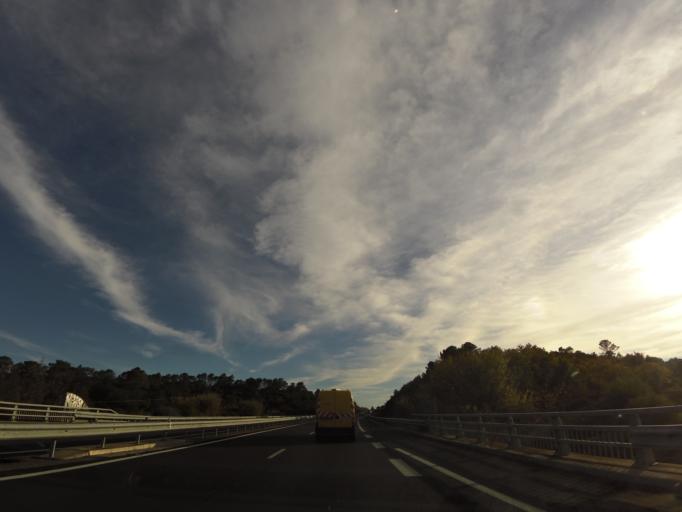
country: FR
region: Languedoc-Roussillon
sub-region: Departement du Gard
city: Vezenobres
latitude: 44.0593
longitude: 4.1229
